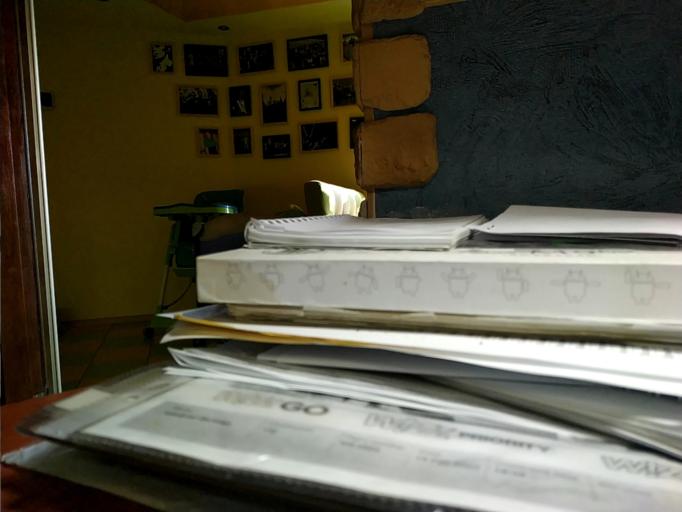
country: RU
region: Novgorod
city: Kholm
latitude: 57.1569
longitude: 31.4235
